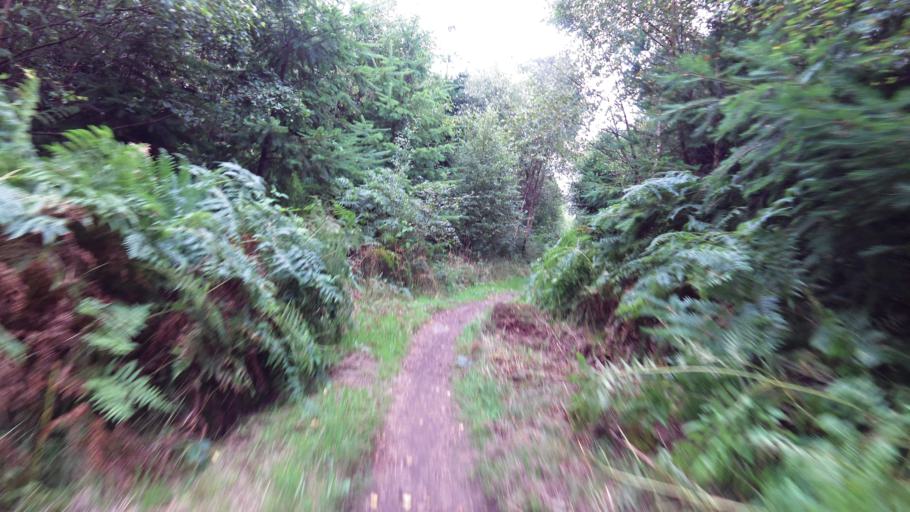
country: GB
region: England
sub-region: North Yorkshire
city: Thornton Dale
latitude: 54.2867
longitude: -0.6875
